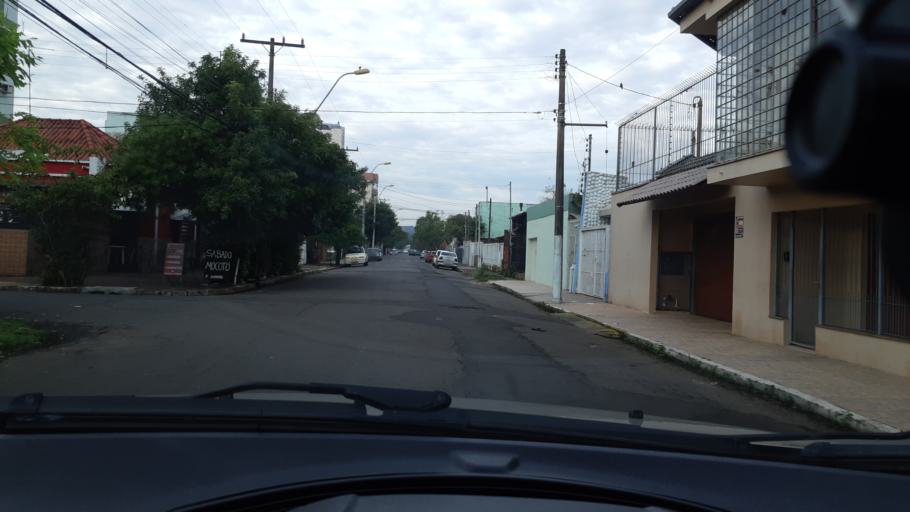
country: BR
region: Rio Grande do Sul
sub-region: Sao Leopoldo
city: Sao Leopoldo
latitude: -29.7674
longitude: -51.1517
